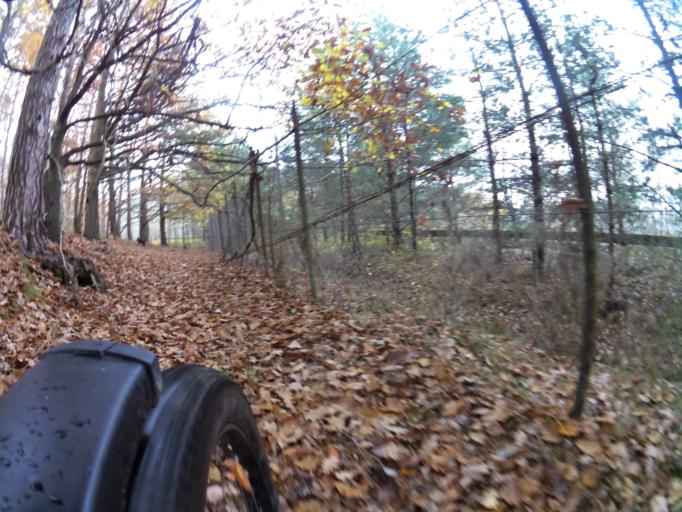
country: PL
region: Pomeranian Voivodeship
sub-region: Powiat pucki
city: Krokowa
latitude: 54.7444
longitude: 18.0979
